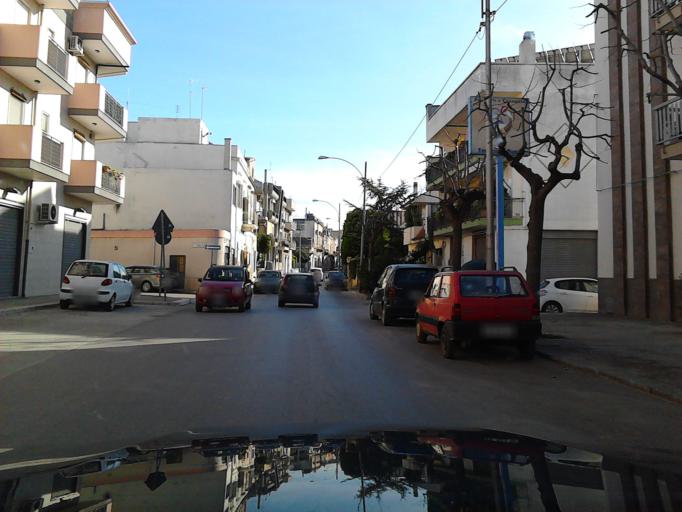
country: IT
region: Apulia
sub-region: Provincia di Bari
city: Rutigliano
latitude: 41.0162
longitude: 17.0003
